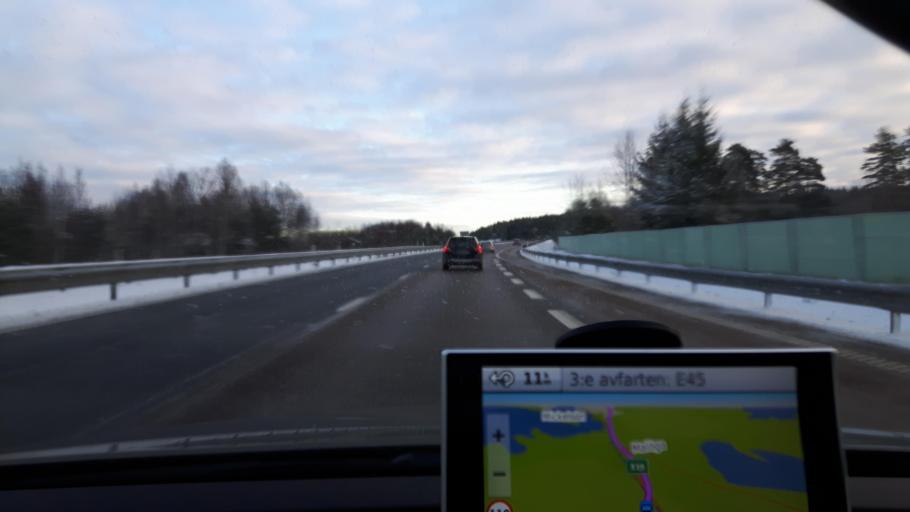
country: SE
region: Vaermland
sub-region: Grums Kommun
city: Slottsbron
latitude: 59.2880
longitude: 13.0505
